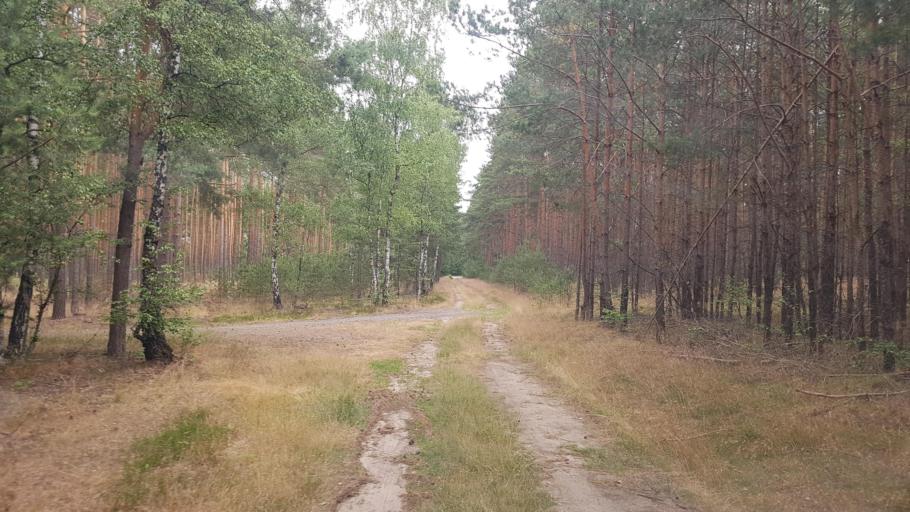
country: DE
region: Brandenburg
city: Treuenbrietzen
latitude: 52.0560
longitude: 12.8178
